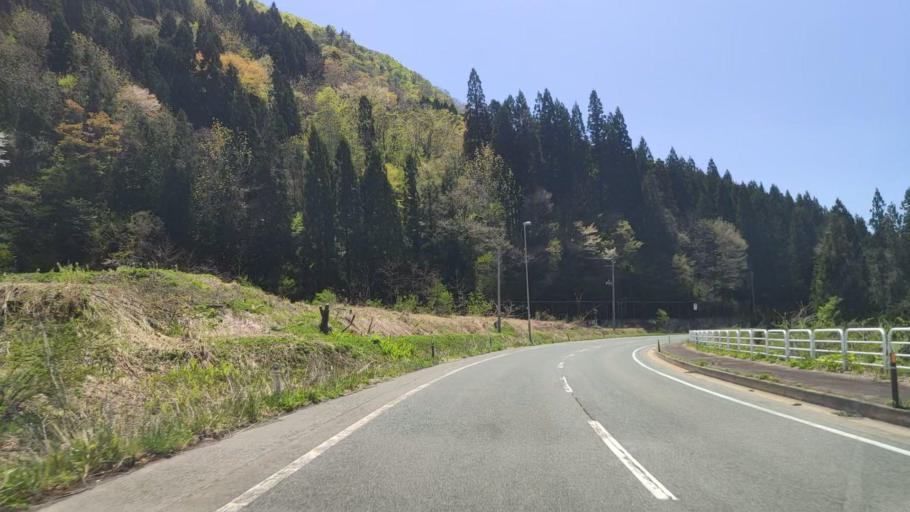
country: JP
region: Yamagata
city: Shinjo
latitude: 38.8979
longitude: 140.3278
